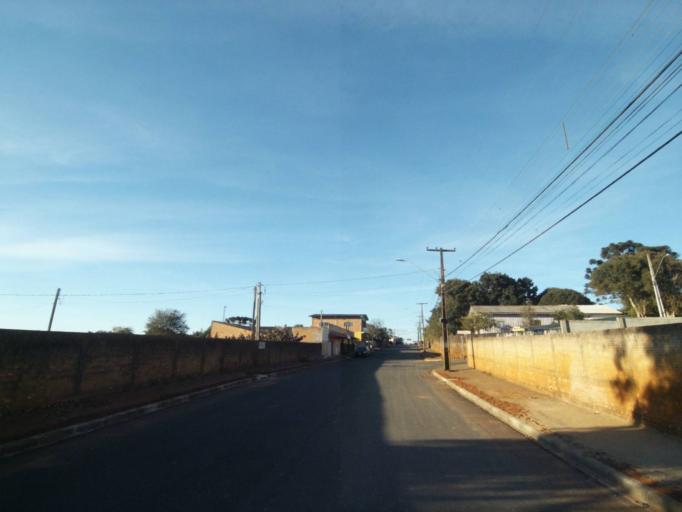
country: BR
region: Parana
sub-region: Tibagi
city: Tibagi
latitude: -24.5206
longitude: -50.4146
